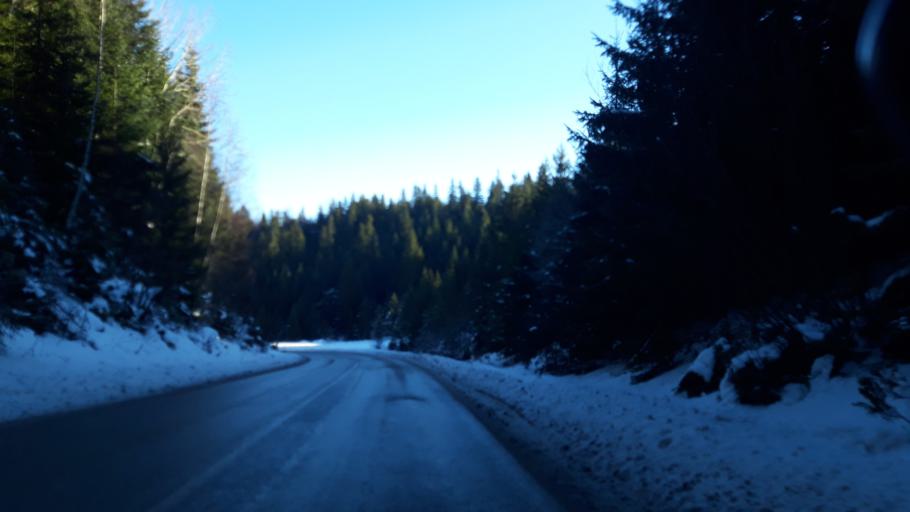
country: BA
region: Republika Srpska
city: Koran
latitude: 43.7889
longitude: 18.5547
